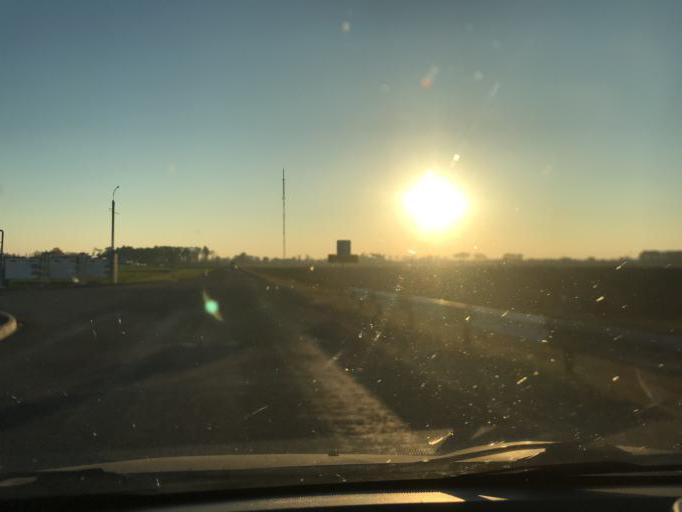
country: BY
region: Gomel
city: Brahin
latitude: 51.8044
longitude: 30.2743
